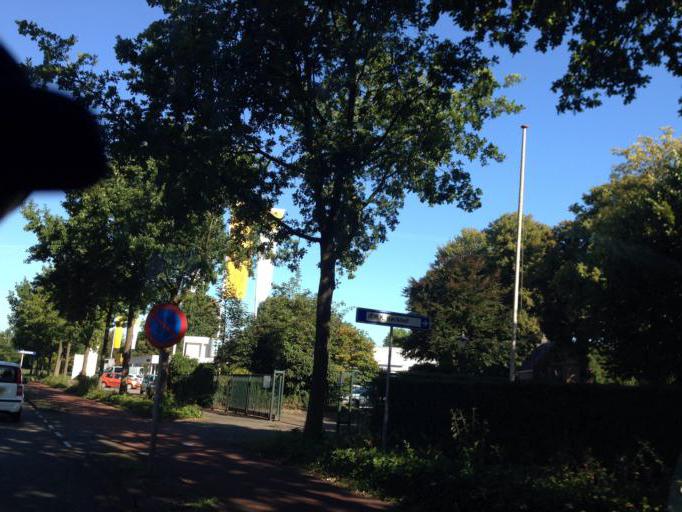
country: NL
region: Overijssel
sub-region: Gemeente Zwolle
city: Zwolle
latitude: 52.5181
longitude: 6.1047
